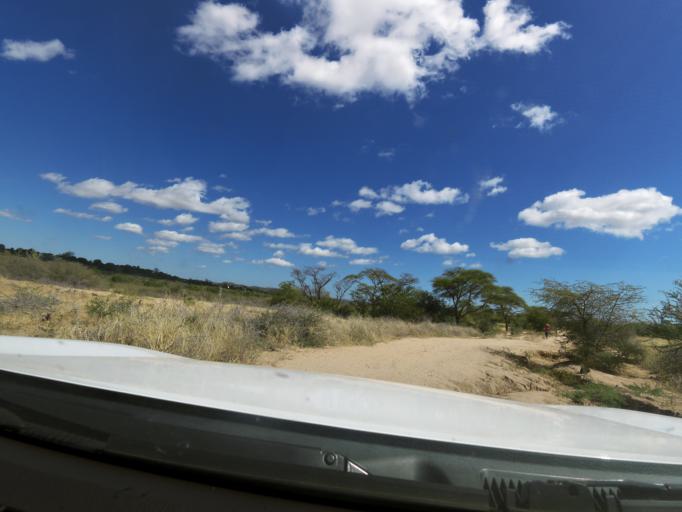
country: ZW
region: Matabeleland North
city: Kamativi Mine
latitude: -17.9991
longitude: 27.1367
